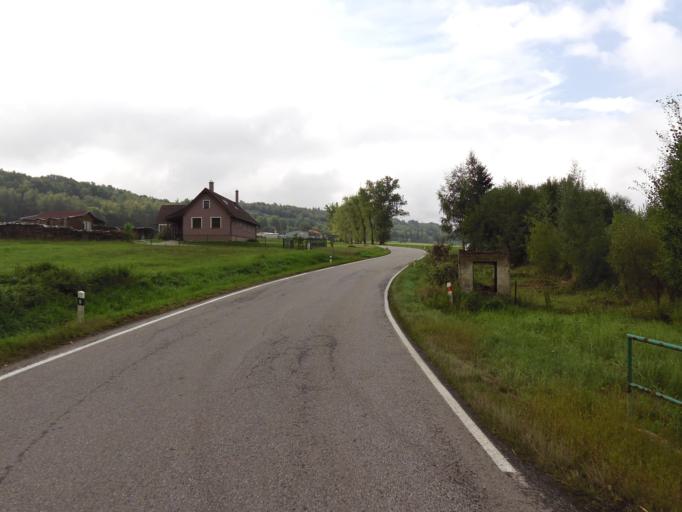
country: CZ
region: Jihocesky
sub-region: Okres Ceske Budejovice
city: Nove Hrady
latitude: 48.8010
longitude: 14.7930
